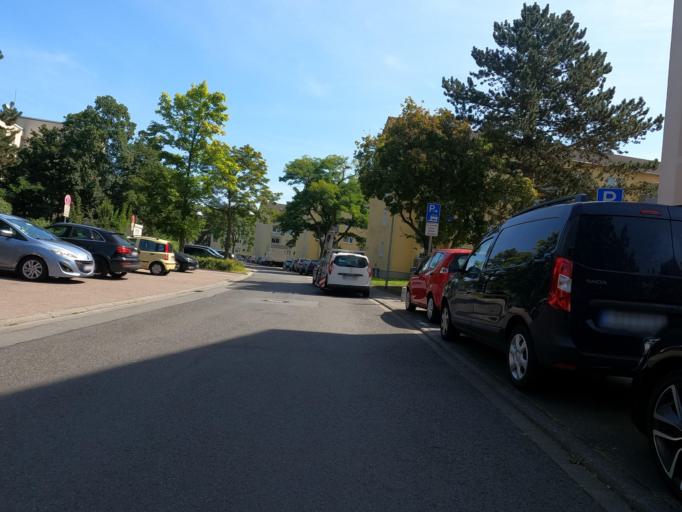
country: DE
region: Hesse
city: Dreieich
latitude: 50.0336
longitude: 8.6916
